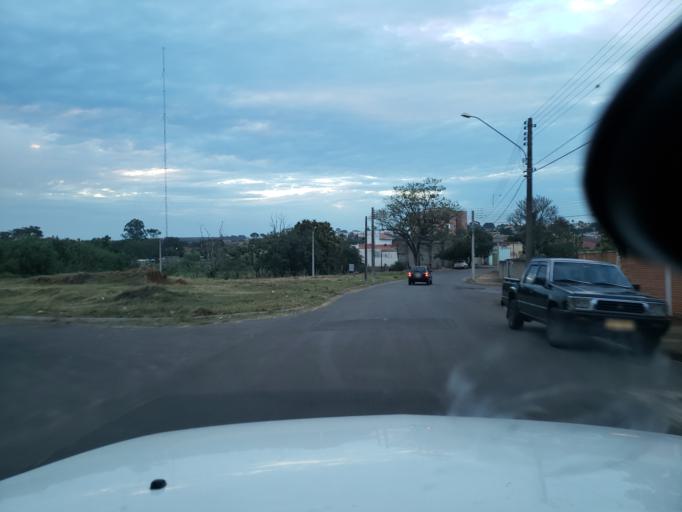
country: BR
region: Sao Paulo
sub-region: Moji-Guacu
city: Mogi-Gaucu
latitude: -22.3666
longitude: -46.9502
